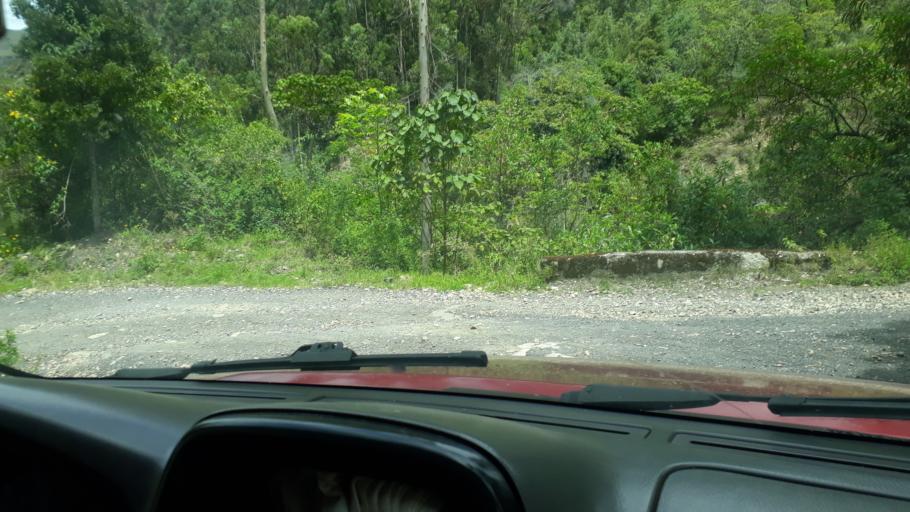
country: CO
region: Boyaca
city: San Mateo
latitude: 6.3975
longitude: -72.5405
